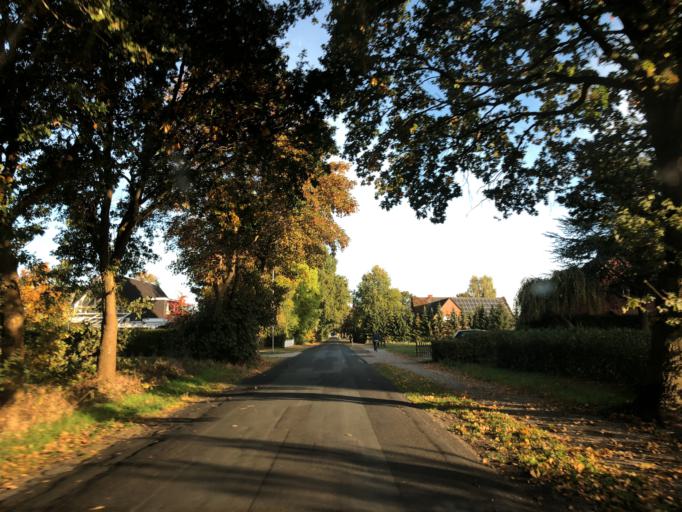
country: DE
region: Lower Saxony
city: Lehe
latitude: 53.0413
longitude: 7.3459
